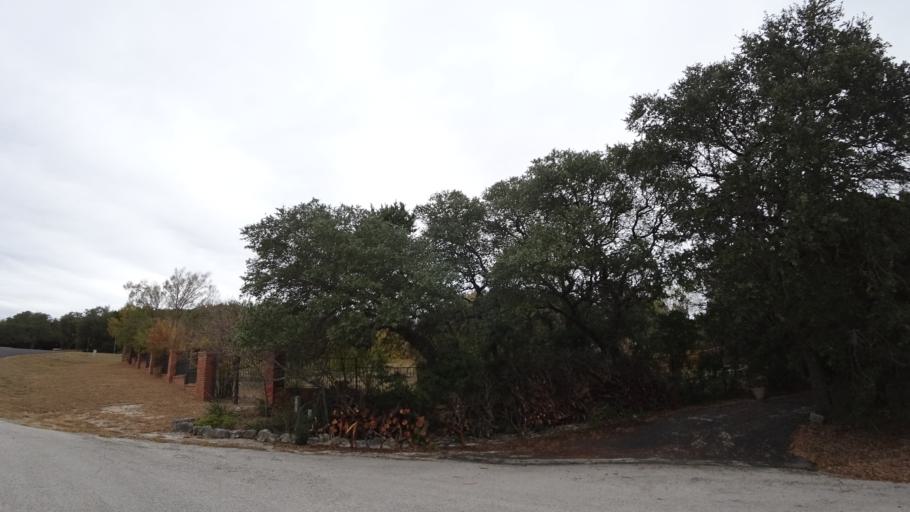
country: US
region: Texas
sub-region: Williamson County
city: Jollyville
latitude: 30.3748
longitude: -97.8077
